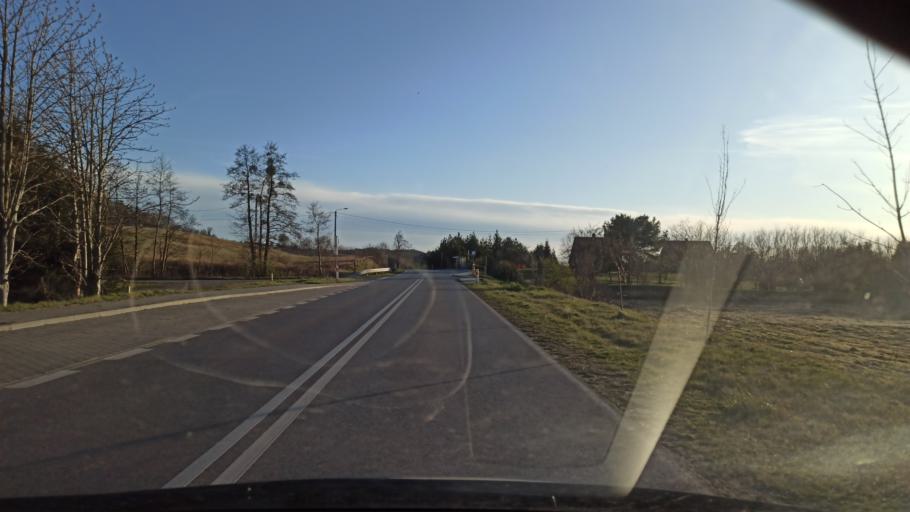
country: PL
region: Warmian-Masurian Voivodeship
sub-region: Powiat elblaski
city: Tolkmicko
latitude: 54.3077
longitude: 19.5135
